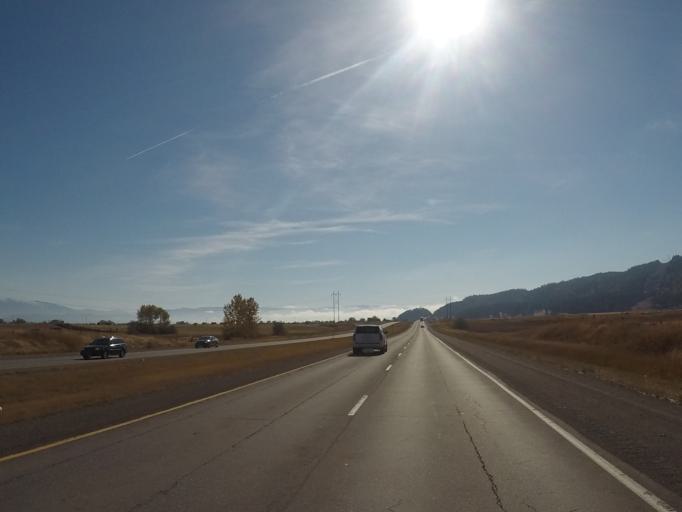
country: US
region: Montana
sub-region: Flathead County
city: Somers
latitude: 48.1153
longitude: -114.2539
